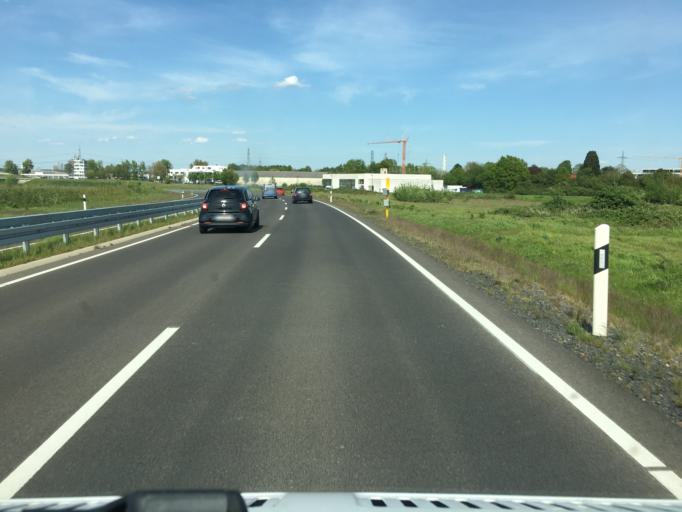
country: DE
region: North Rhine-Westphalia
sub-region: Regierungsbezirk Koln
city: Hurth
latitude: 50.8756
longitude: 6.9014
